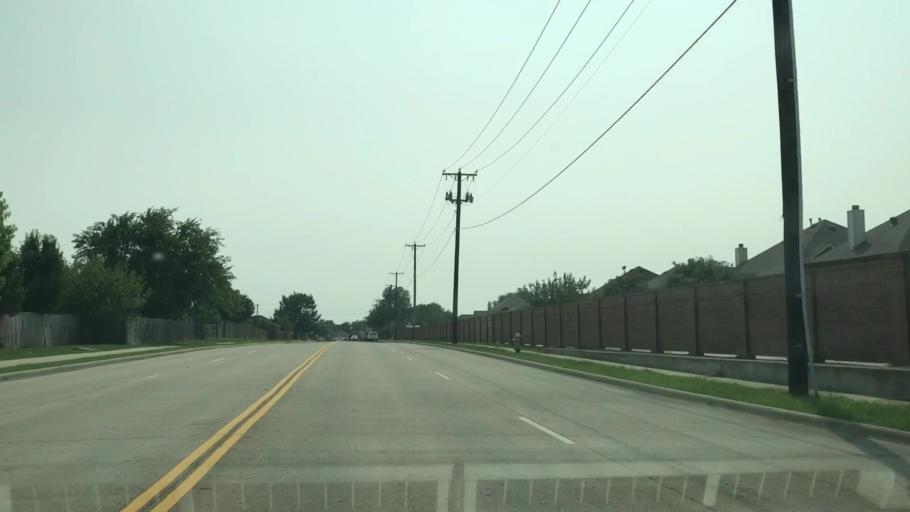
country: US
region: Texas
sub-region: Dallas County
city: Rowlett
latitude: 32.9245
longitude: -96.5760
